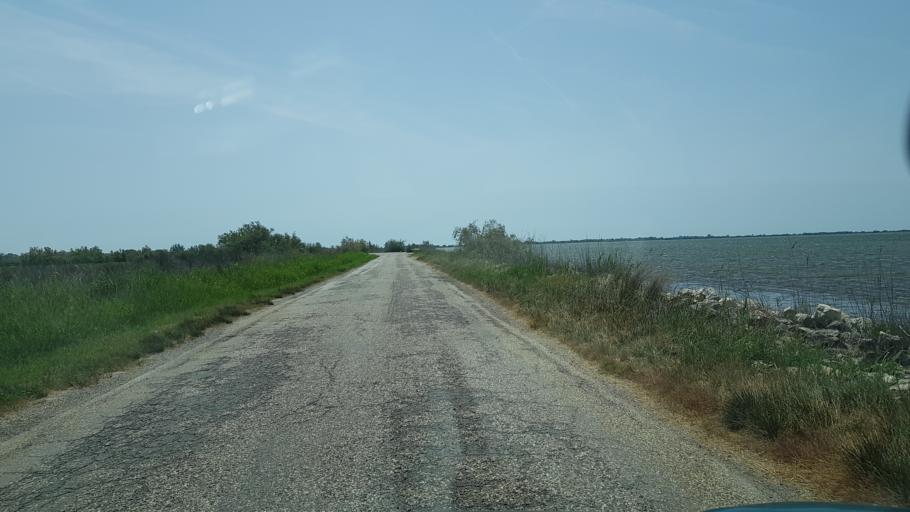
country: FR
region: Provence-Alpes-Cote d'Azur
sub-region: Departement des Bouches-du-Rhone
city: Arles
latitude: 43.5442
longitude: 4.6320
